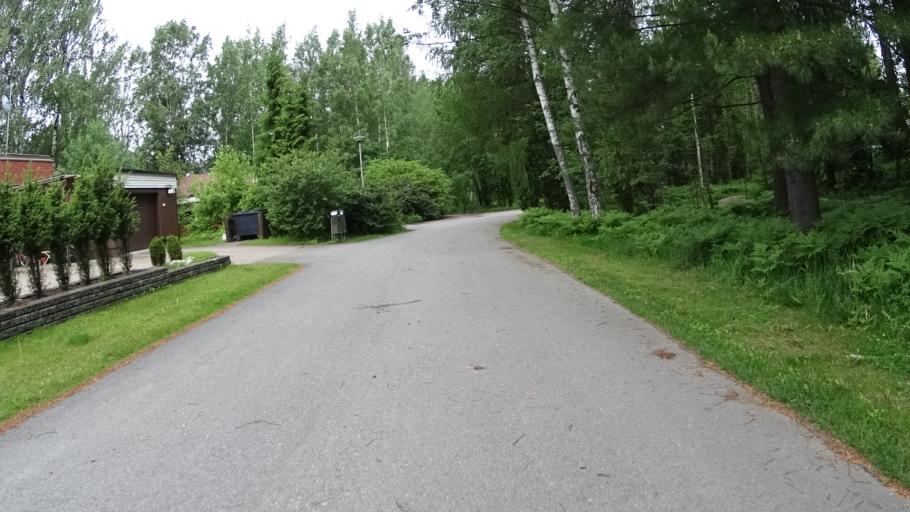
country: FI
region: Uusimaa
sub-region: Helsinki
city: Koukkuniemi
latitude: 60.1720
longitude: 24.7856
